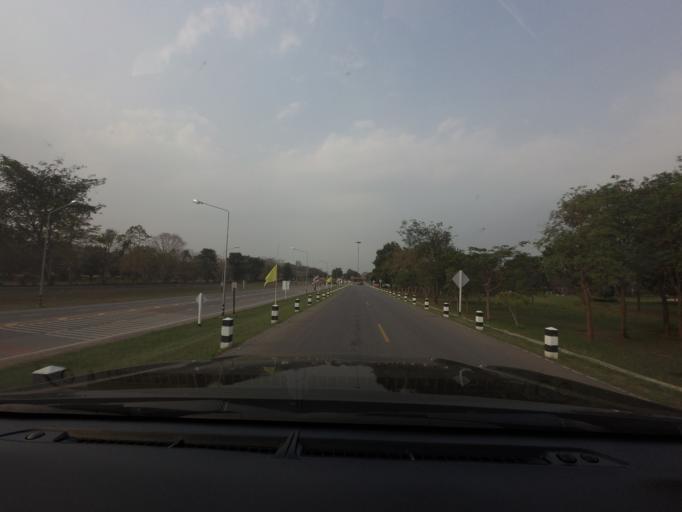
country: TH
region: Sara Buri
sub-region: Amphoe Wang Muang
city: Wang Muang
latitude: 14.8638
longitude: 101.0626
